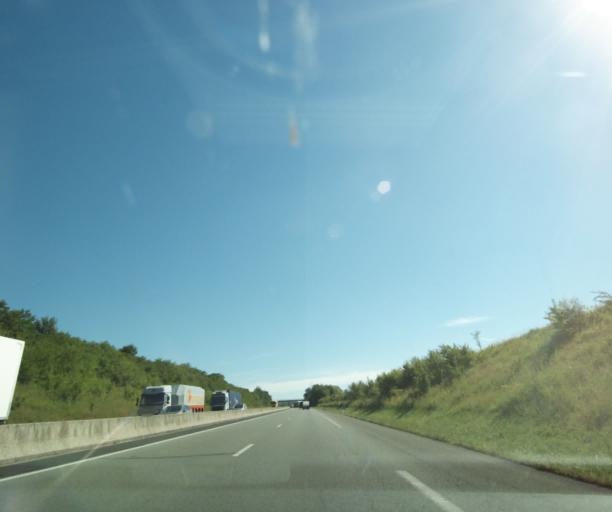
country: FR
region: Champagne-Ardenne
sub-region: Departement de la Haute-Marne
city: Avrecourt
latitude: 48.0420
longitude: 5.5658
